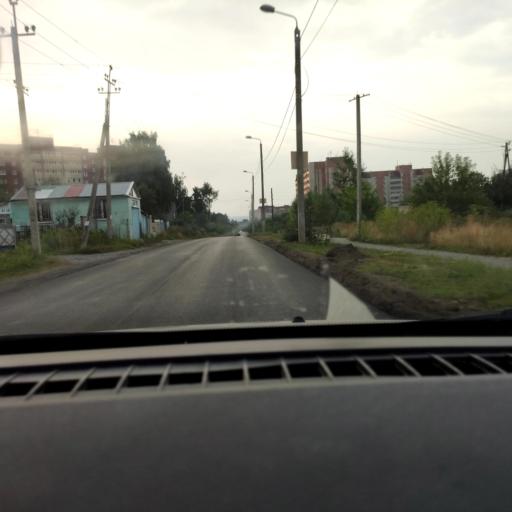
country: RU
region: Perm
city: Perm
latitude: 58.1027
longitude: 56.2908
